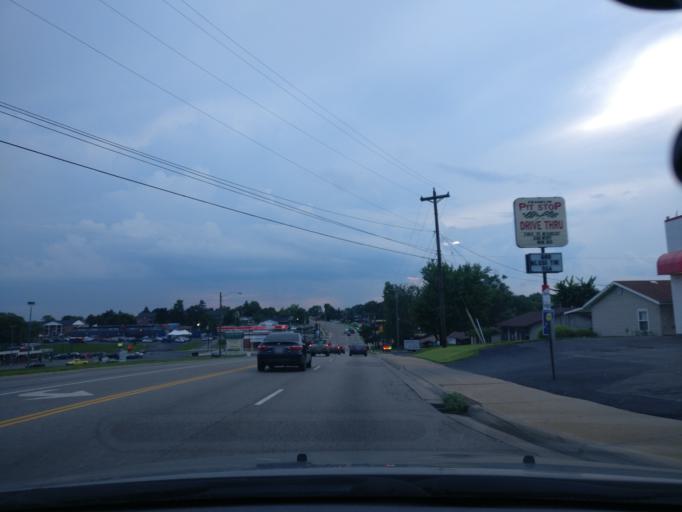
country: US
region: Ohio
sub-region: Warren County
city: Franklin
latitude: 39.5639
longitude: -84.2817
